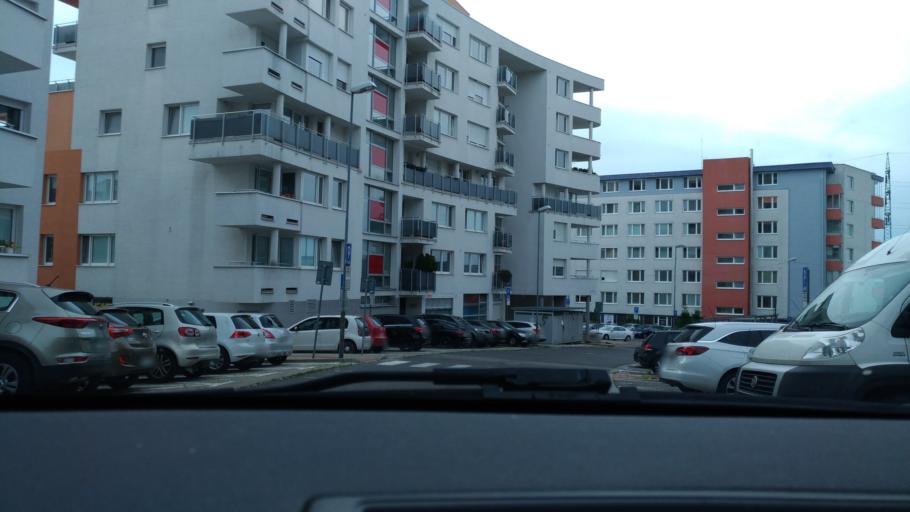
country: AT
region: Lower Austria
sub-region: Politischer Bezirk Bruck an der Leitha
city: Berg
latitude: 48.1500
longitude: 17.0504
